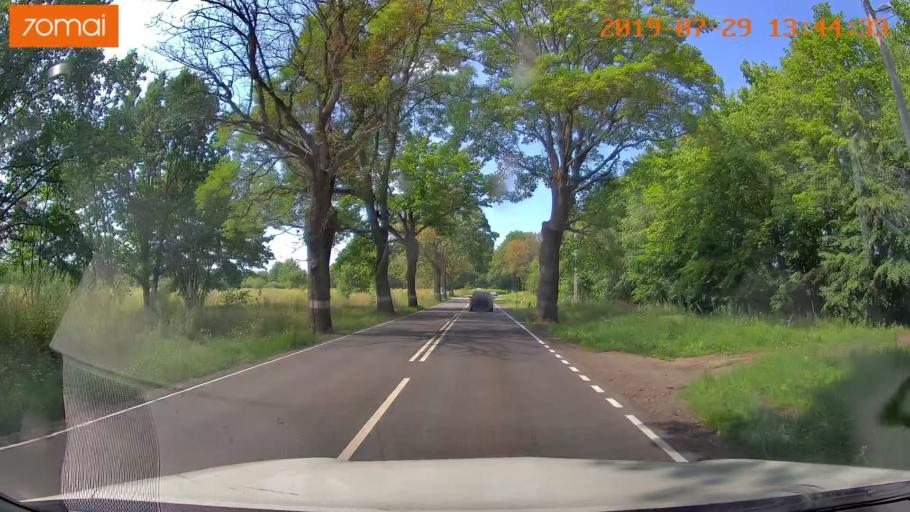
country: RU
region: Kaliningrad
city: Svetlyy
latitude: 54.7379
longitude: 20.0866
